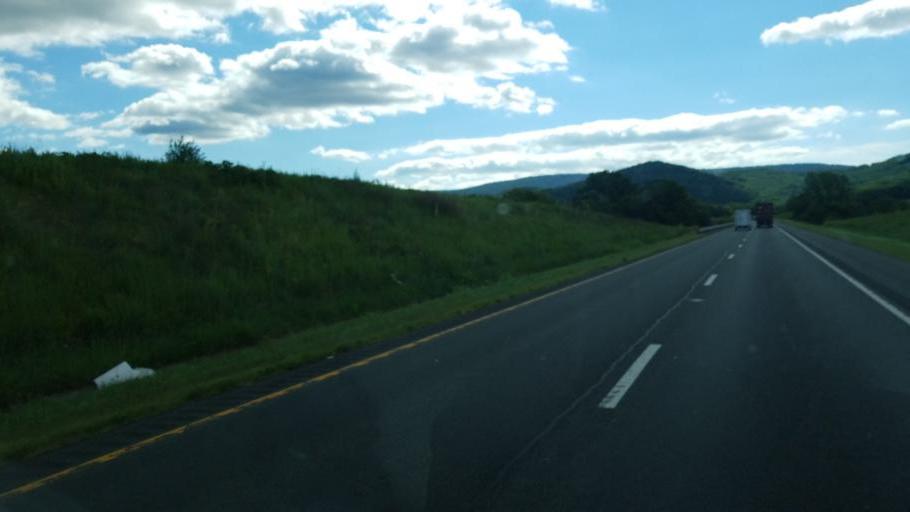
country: US
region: Virginia
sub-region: Warren County
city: Apple Mountain Lake
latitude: 38.9449
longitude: -78.1465
